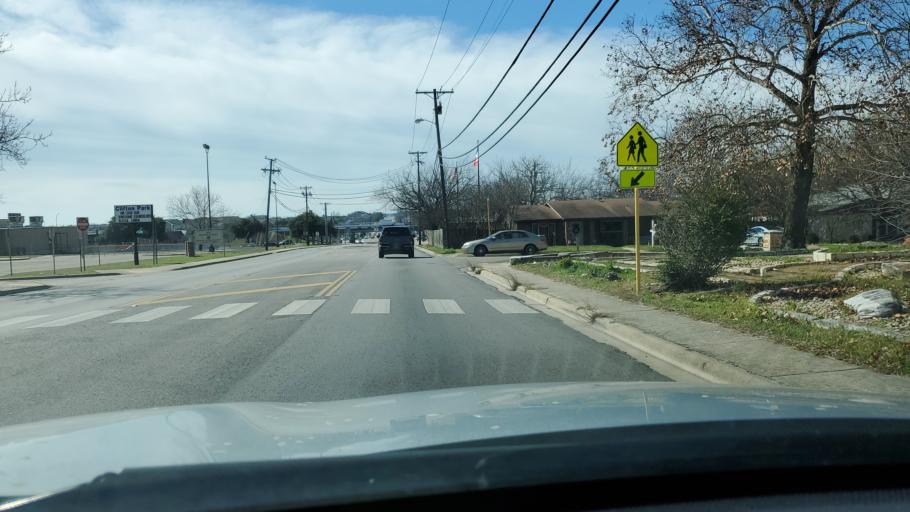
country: US
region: Texas
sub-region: Bell County
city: Killeen
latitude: 31.0976
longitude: -97.7314
